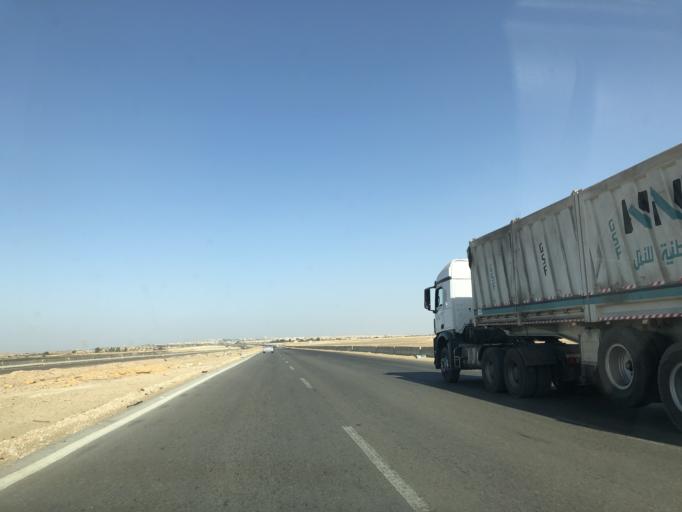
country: EG
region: Muhafazat al Minufiyah
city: Ashmun
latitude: 30.0677
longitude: 30.8920
